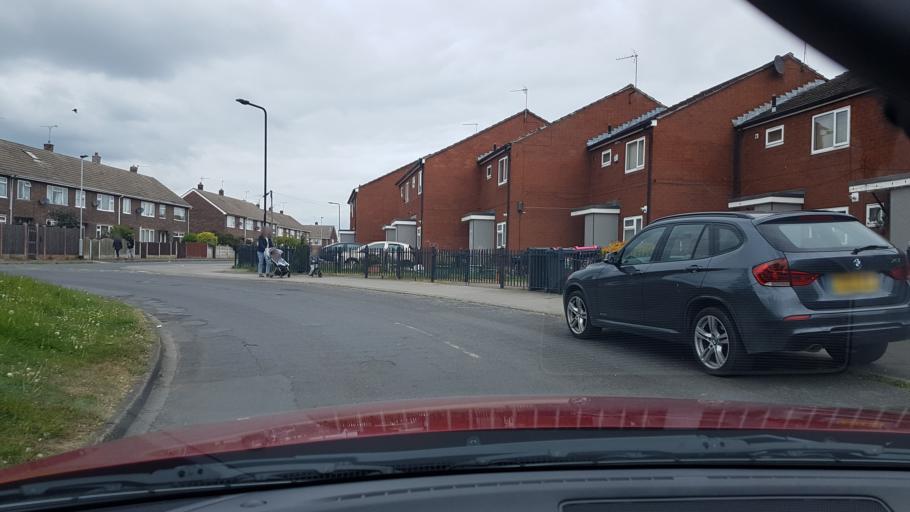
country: GB
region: England
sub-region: Rotherham
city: Maltby
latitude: 53.4169
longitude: -1.1892
